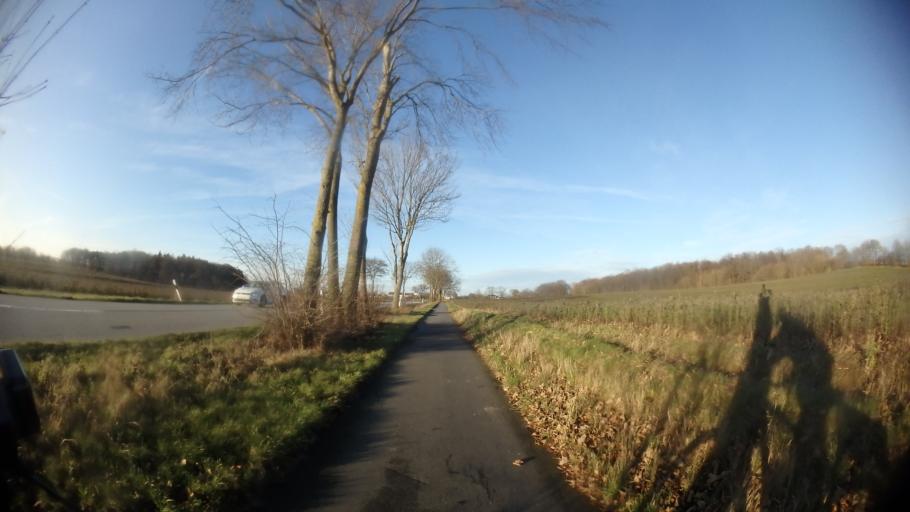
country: DE
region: Schleswig-Holstein
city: Travemuende
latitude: 53.9820
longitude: 10.8457
